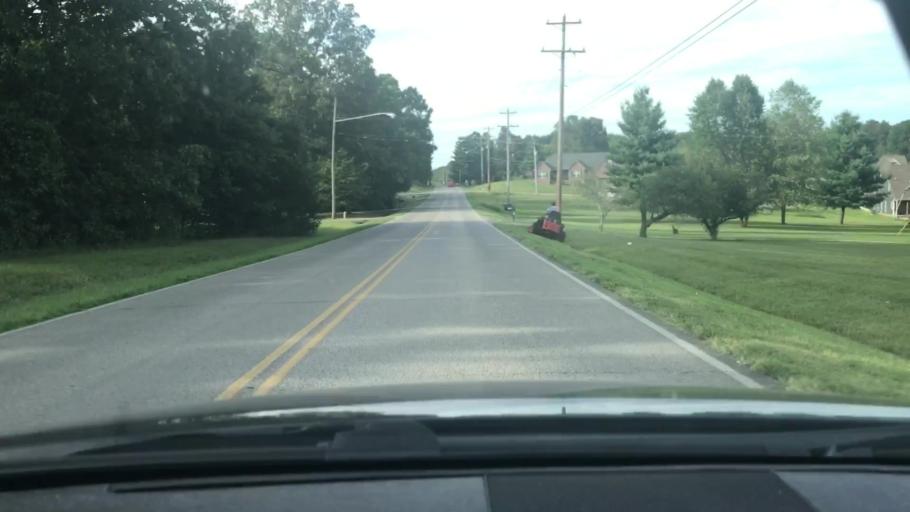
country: US
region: Tennessee
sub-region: Dickson County
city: White Bluff
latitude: 36.0928
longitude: -87.2138
